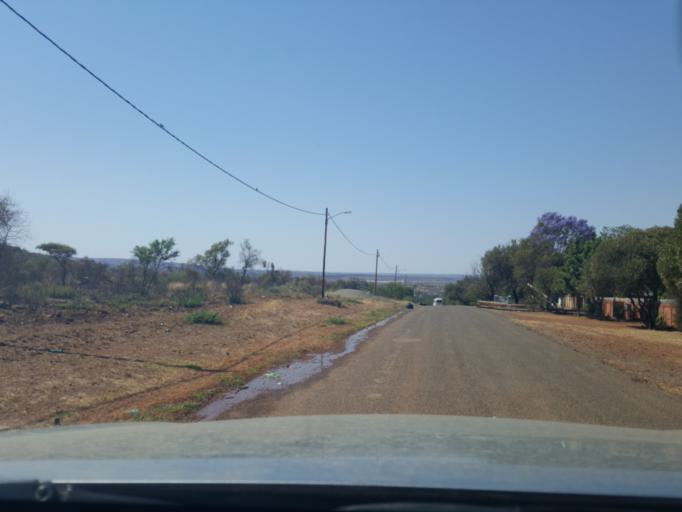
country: ZA
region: North-West
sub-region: Ngaka Modiri Molema District Municipality
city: Zeerust
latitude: -25.5314
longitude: 26.0813
